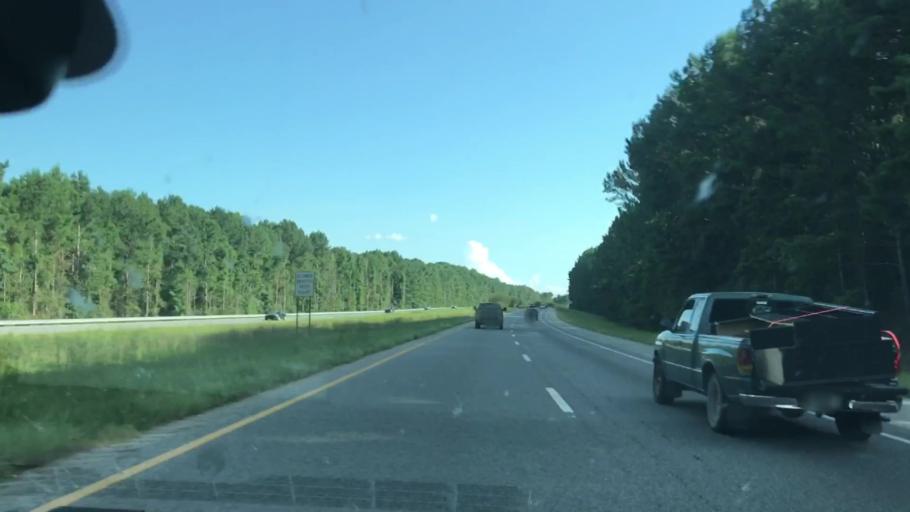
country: US
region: Georgia
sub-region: Harris County
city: Pine Mountain
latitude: 32.9288
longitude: -84.9488
